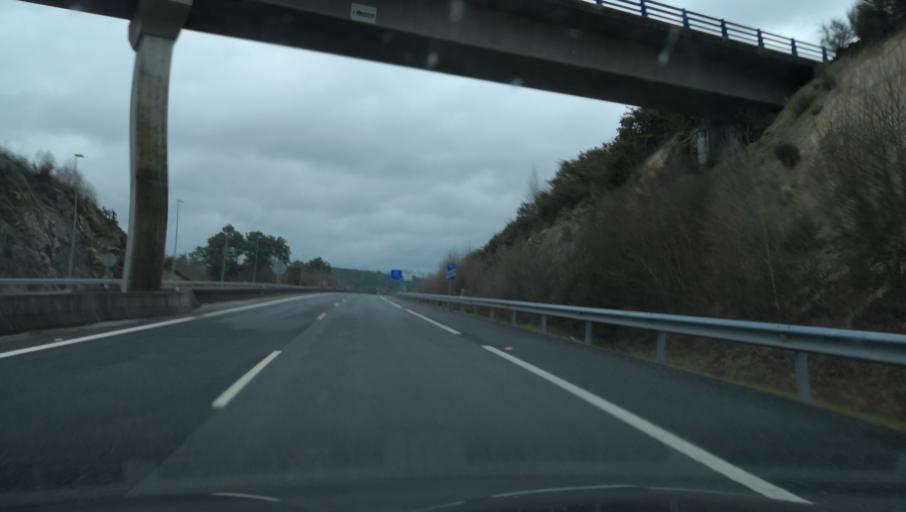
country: ES
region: Galicia
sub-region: Provincia de Ourense
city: Pinor
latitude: 42.5189
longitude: -8.0194
